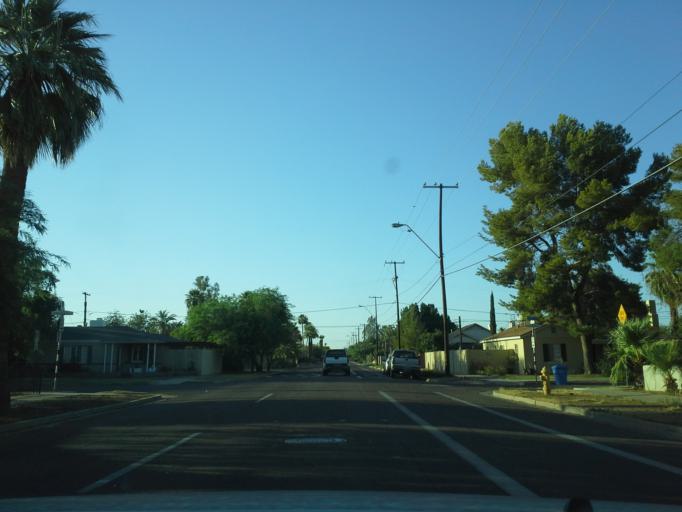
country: US
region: Arizona
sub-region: Maricopa County
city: Phoenix
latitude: 33.4672
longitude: -112.0783
